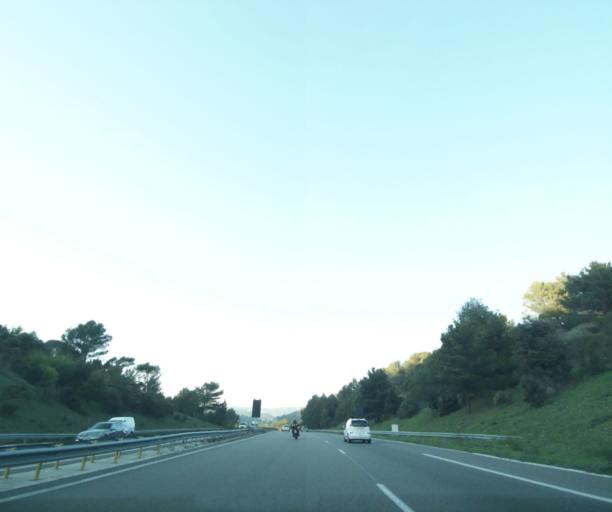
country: FR
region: Provence-Alpes-Cote d'Azur
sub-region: Departement des Bouches-du-Rhone
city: Roquevaire
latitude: 43.3545
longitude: 5.6206
